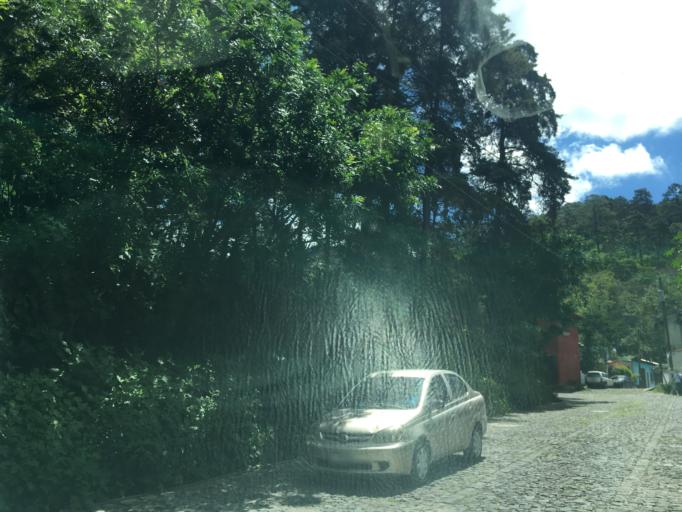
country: GT
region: Sacatepequez
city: Antigua Guatemala
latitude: 14.5667
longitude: -90.7267
